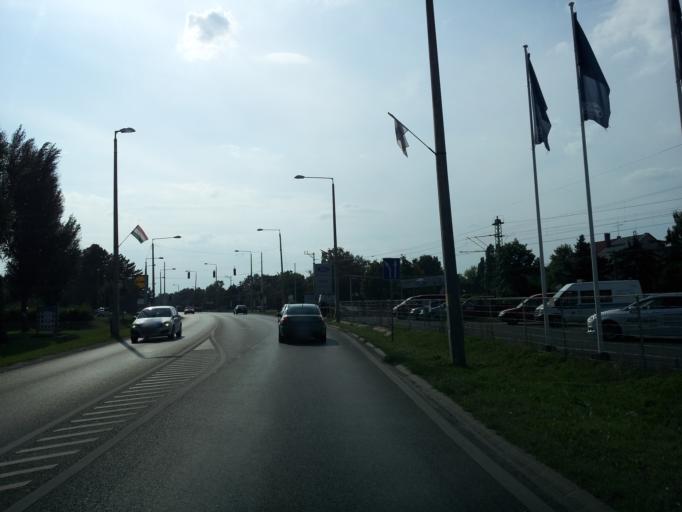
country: HU
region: Somogy
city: Siofok
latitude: 46.9004
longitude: 18.0295
